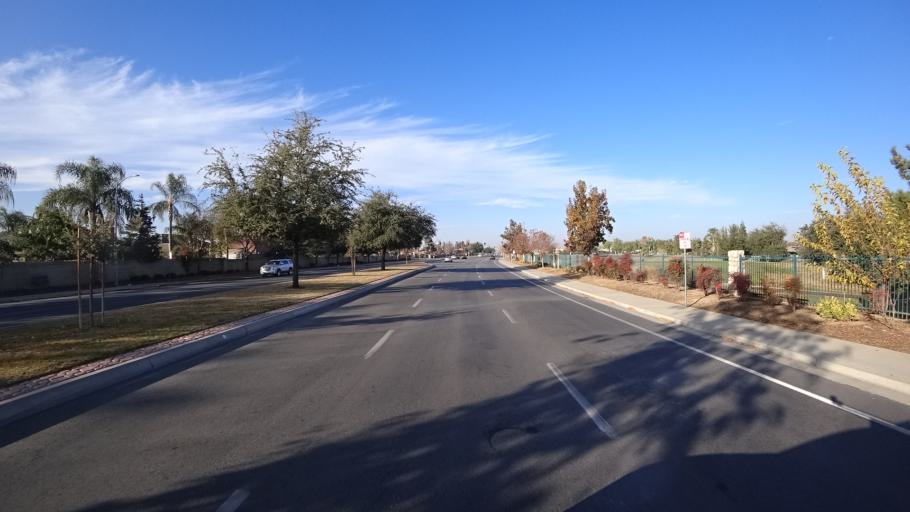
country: US
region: California
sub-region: Kern County
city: Greenacres
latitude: 35.3981
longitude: -119.1037
